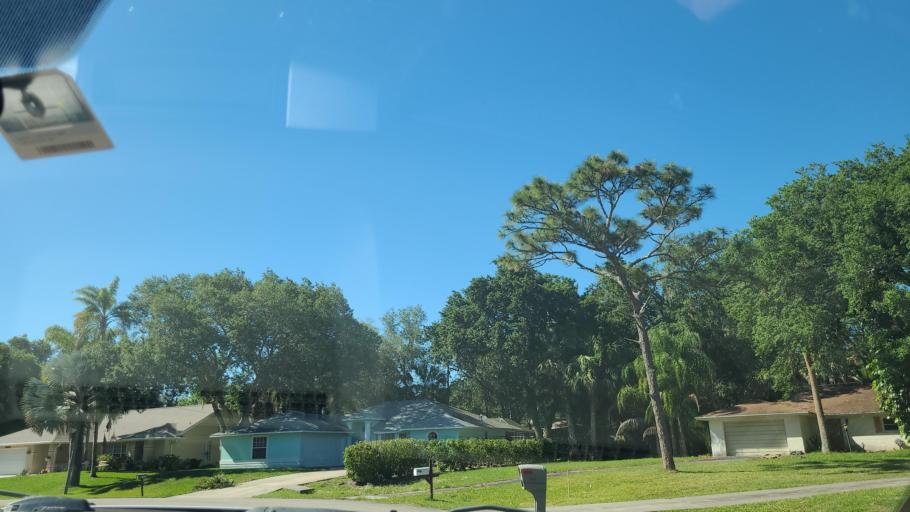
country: US
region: Florida
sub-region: Indian River County
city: Sebastian
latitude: 27.7626
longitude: -80.4999
